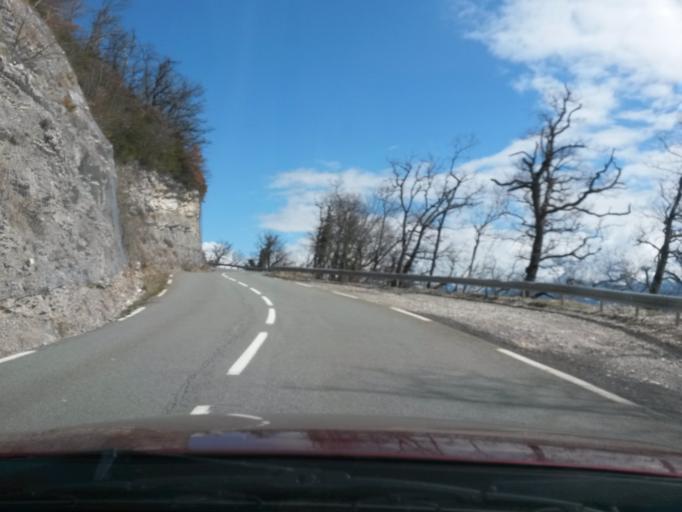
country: FR
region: Rhone-Alpes
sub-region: Departement de l'Isere
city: Bernin
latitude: 45.2790
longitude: 5.8447
